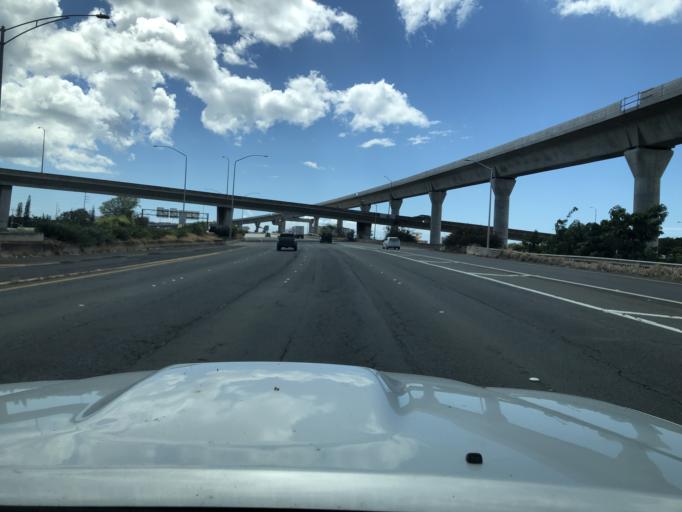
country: US
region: Hawaii
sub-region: Honolulu County
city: Hickam Field
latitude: 21.3438
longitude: -157.9330
